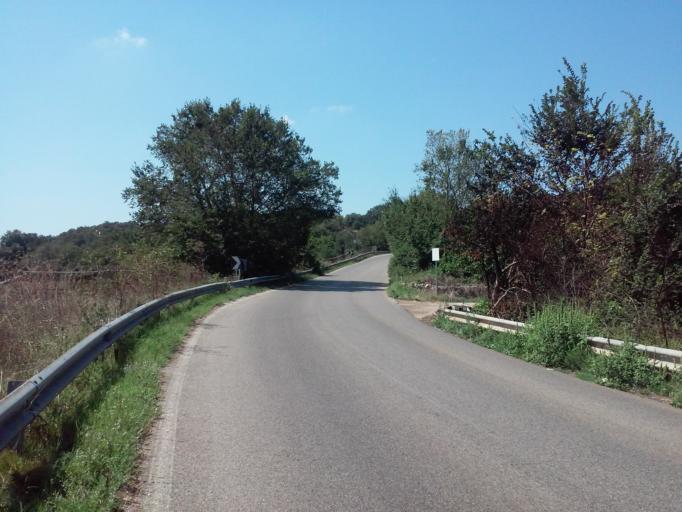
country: IT
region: Apulia
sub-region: Provincia di Bari
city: Alberobello
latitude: 40.8049
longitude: 17.1971
